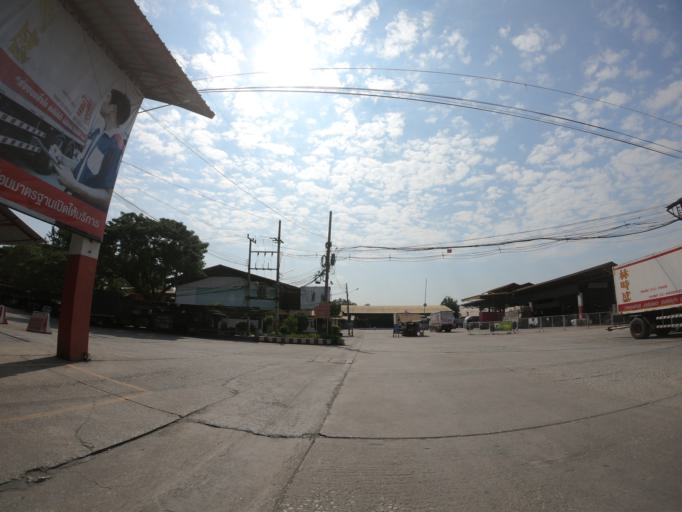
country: TH
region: Chiang Mai
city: Chiang Mai
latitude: 18.8086
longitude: 99.0093
